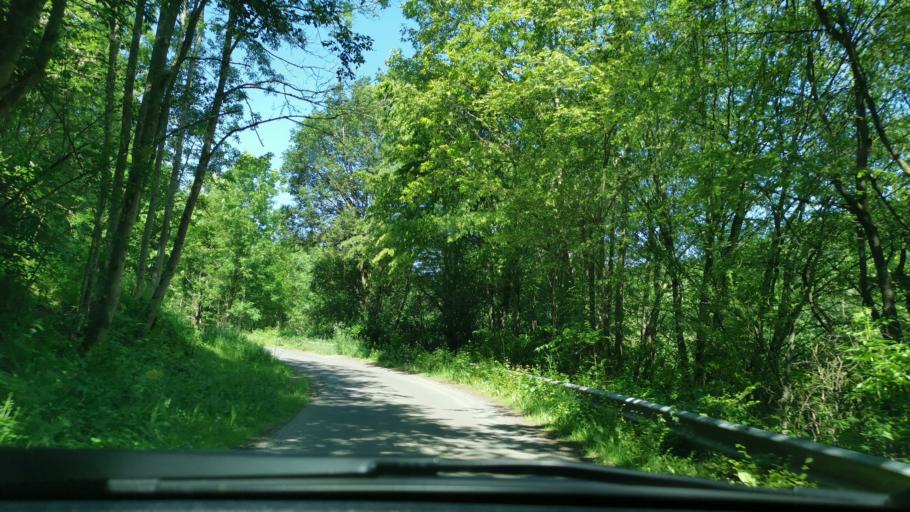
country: DE
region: Hesse
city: Waldkappel
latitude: 51.1776
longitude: 9.8132
